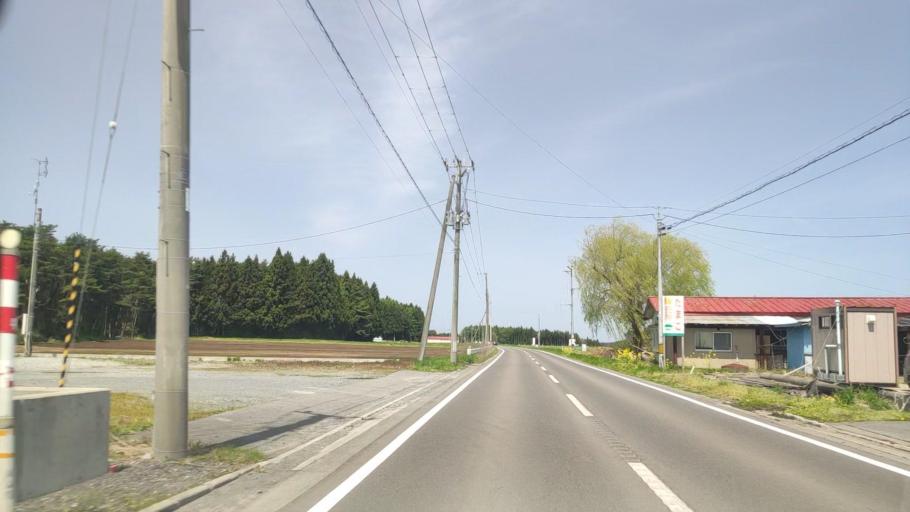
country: JP
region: Aomori
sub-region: Hachinohe Shi
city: Uchimaru
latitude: 40.5379
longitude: 141.4014
